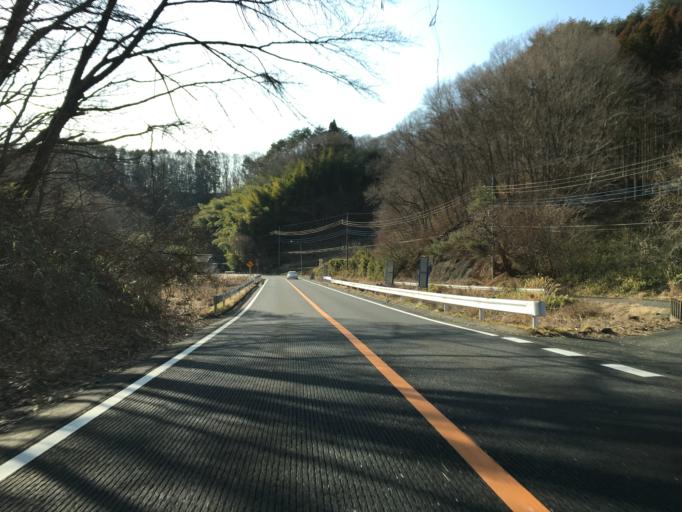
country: JP
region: Ibaraki
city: Takahagi
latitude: 36.7384
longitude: 140.5491
